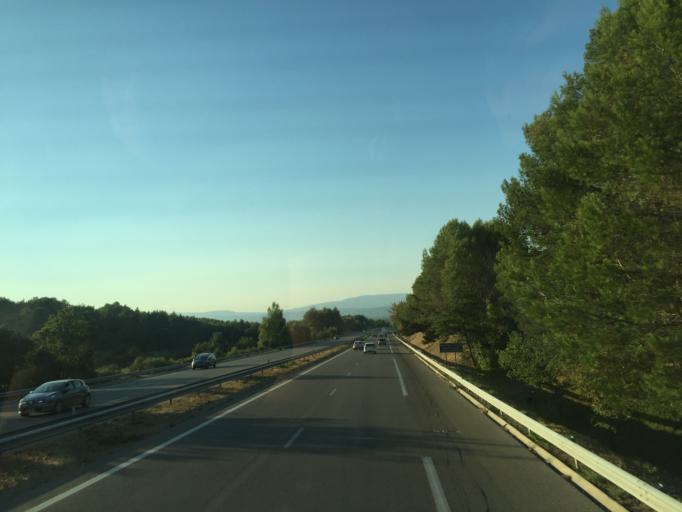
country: FR
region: Provence-Alpes-Cote d'Azur
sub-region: Departement des Bouches-du-Rhone
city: Venelles
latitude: 43.6153
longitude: 5.4964
